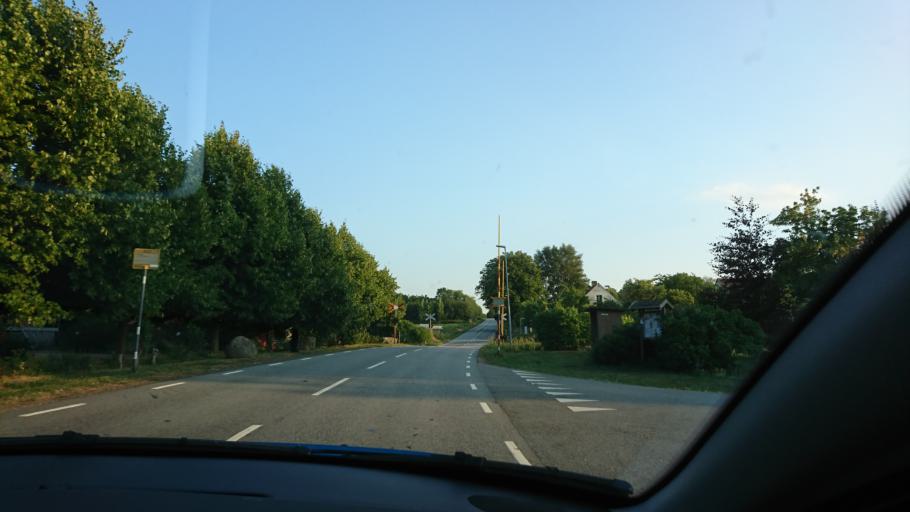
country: SE
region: Skane
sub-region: Simrishamns Kommun
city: Kivik
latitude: 55.7084
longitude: 14.1520
